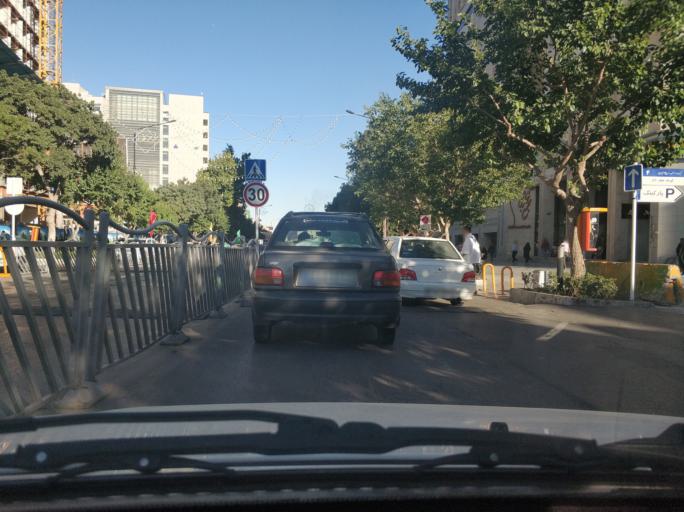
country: IR
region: Razavi Khorasan
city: Mashhad
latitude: 36.2929
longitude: 59.6112
